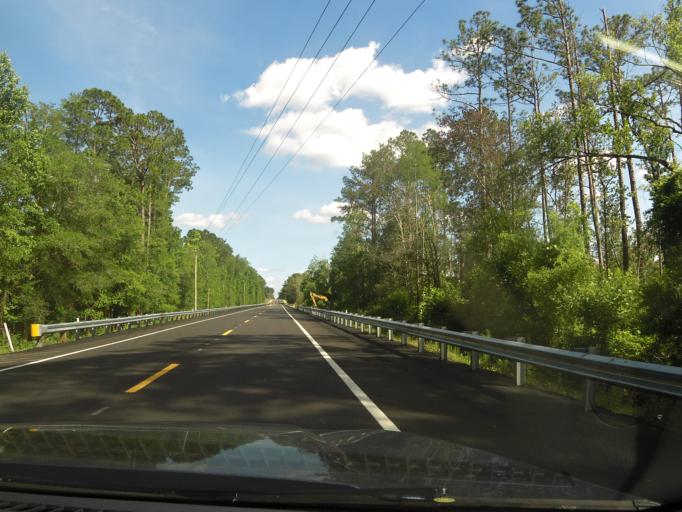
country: US
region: Florida
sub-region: Nassau County
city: Hilliard
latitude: 30.6320
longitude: -81.8967
